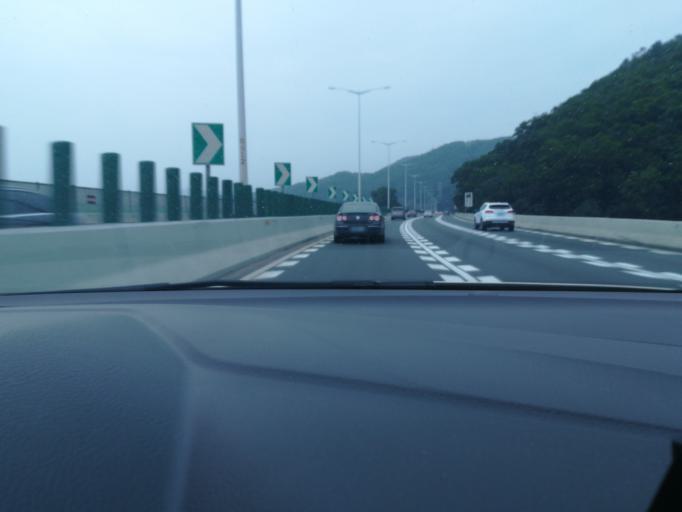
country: CN
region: Guangdong
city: Longdong
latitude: 23.2419
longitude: 113.3512
